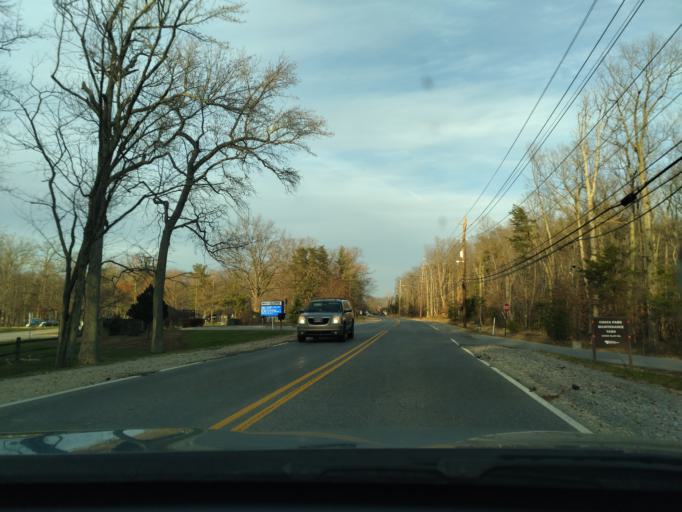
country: US
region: Maryland
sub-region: Prince George's County
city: Clinton
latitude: 38.7394
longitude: -76.9074
